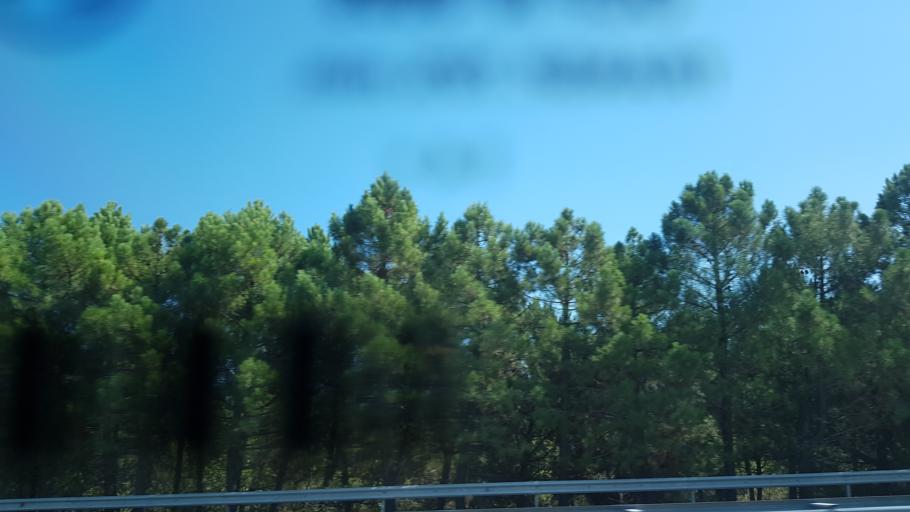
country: TR
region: Kirklareli
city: Luleburgaz
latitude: 41.4464
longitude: 27.3891
